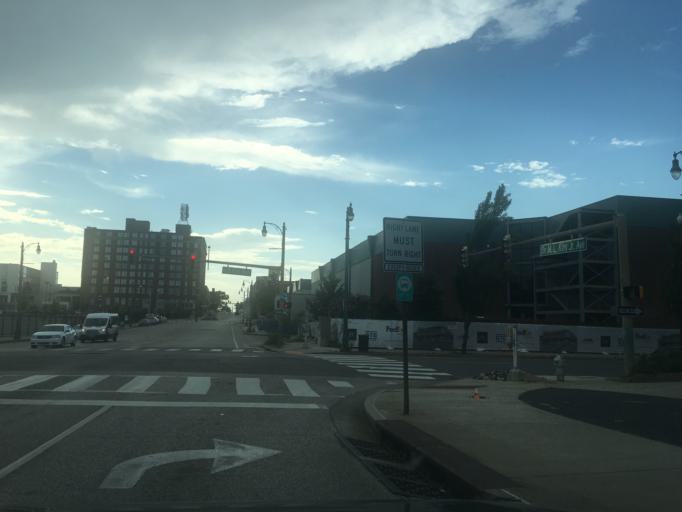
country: US
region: Tennessee
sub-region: Shelby County
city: Memphis
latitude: 35.1374
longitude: -90.0527
